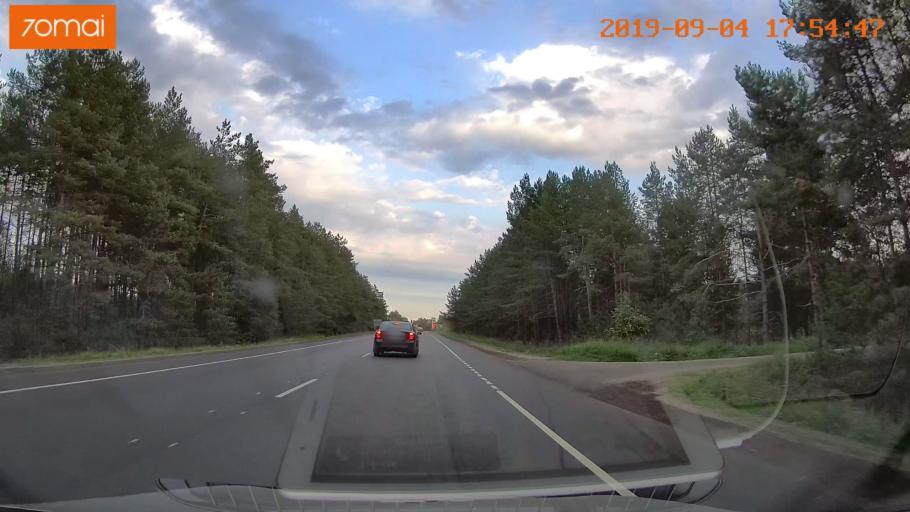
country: RU
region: Moskovskaya
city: Imeni Tsyurupy
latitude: 55.5087
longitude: 38.7545
